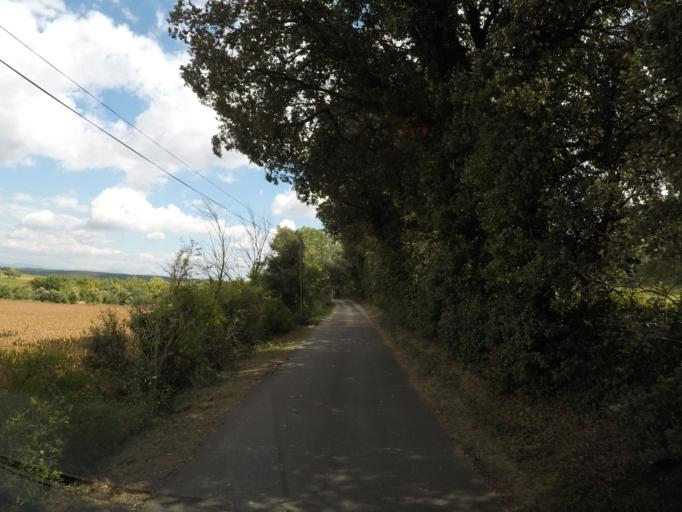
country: FR
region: Rhone-Alpes
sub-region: Departement de la Drome
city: Saint-Restitut
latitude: 44.3057
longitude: 4.7906
